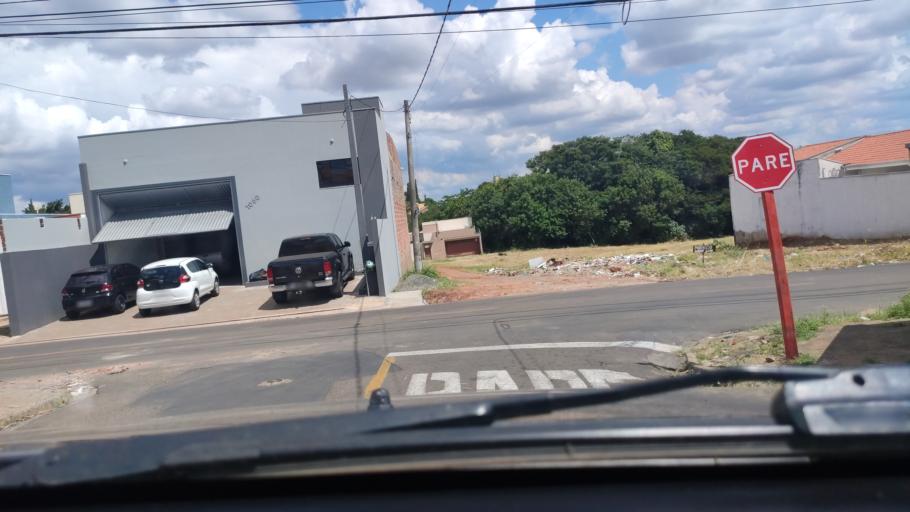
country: BR
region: Sao Paulo
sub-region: Sao Carlos
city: Sao Carlos
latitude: -22.0095
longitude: -47.8736
